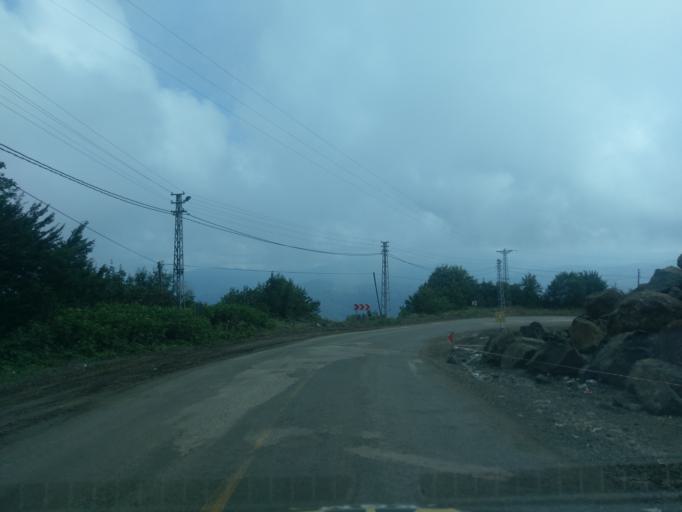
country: TR
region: Ordu
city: Gurgentepe
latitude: 40.8519
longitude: 37.6601
